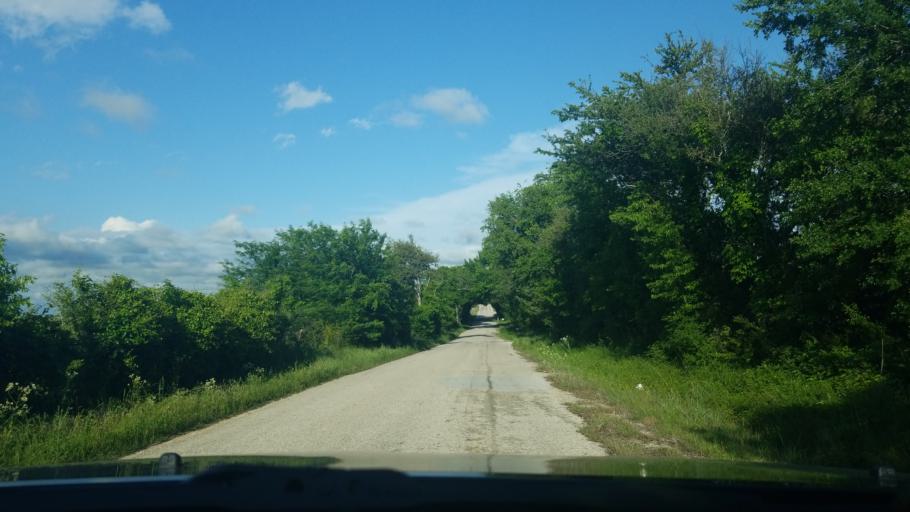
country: US
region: Texas
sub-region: Wise County
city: Decatur
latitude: 33.2429
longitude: -97.4923
